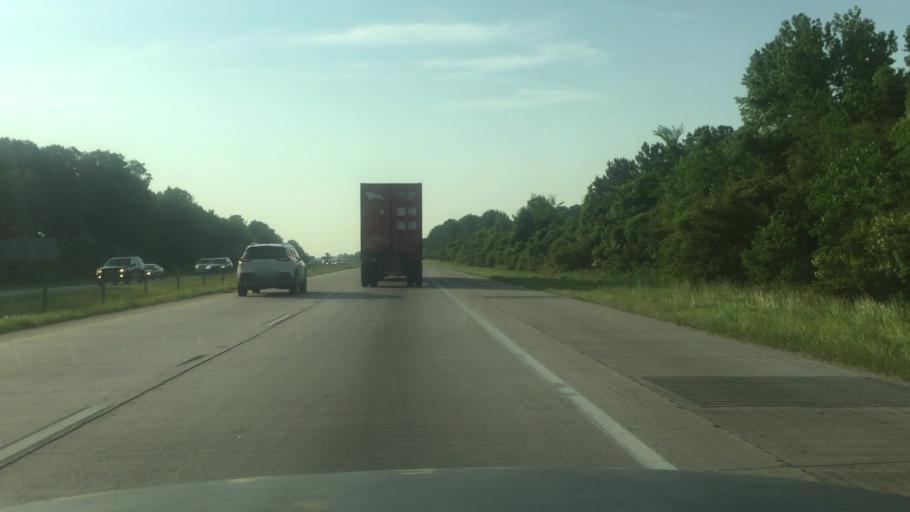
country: US
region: South Carolina
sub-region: Charleston County
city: Mount Pleasant
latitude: 32.8477
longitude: -79.8776
